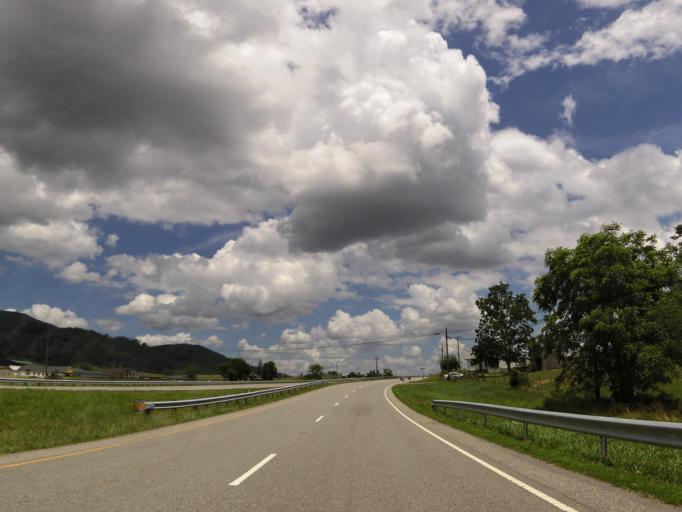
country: US
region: Tennessee
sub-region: Claiborne County
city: Harrogate
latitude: 36.6321
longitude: -83.4887
